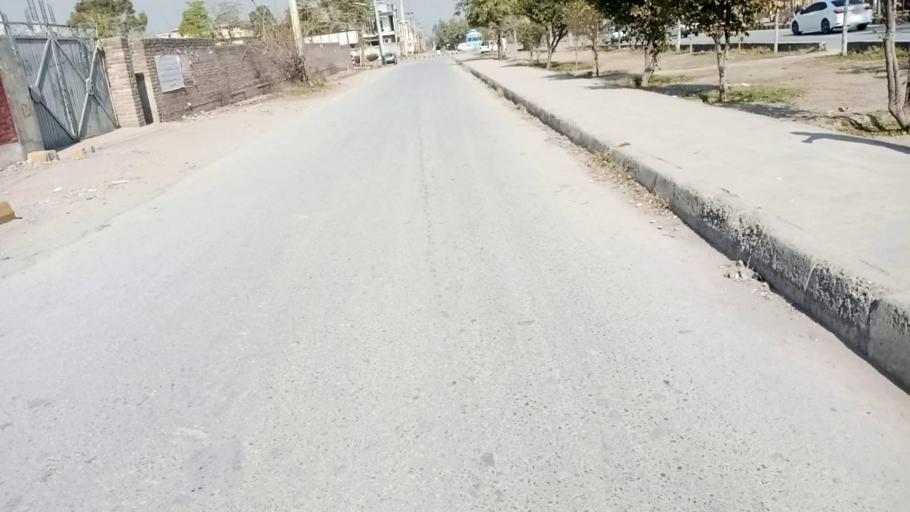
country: PK
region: Khyber Pakhtunkhwa
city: Peshawar
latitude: 33.9554
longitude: 71.4326
